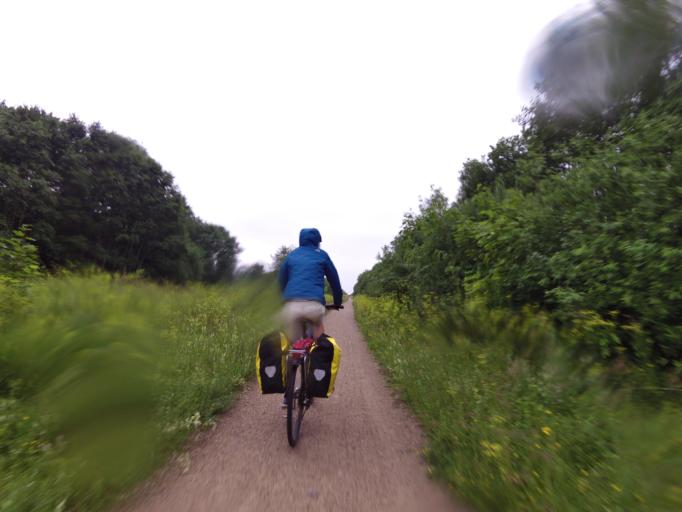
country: EE
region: Harju
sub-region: Nissi vald
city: Turba
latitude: 58.9979
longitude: 24.0522
